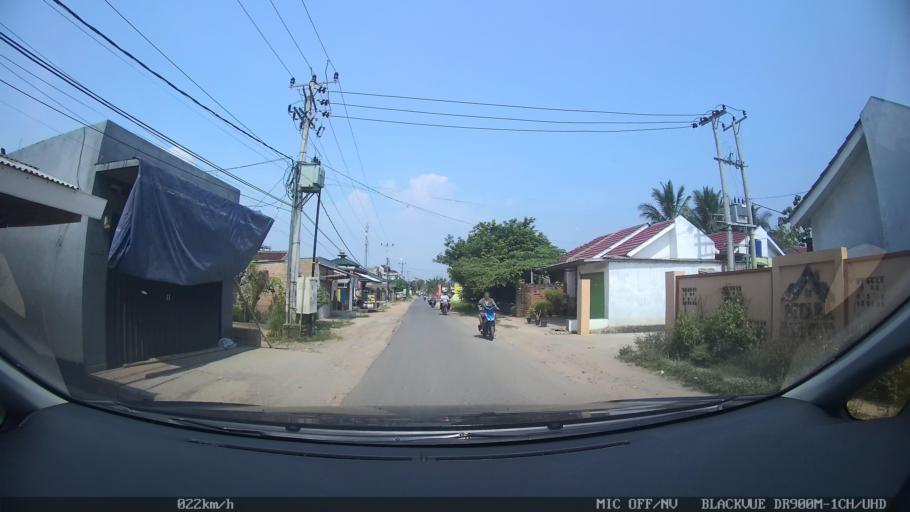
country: ID
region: Lampung
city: Natar
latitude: -5.3096
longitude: 105.2059
